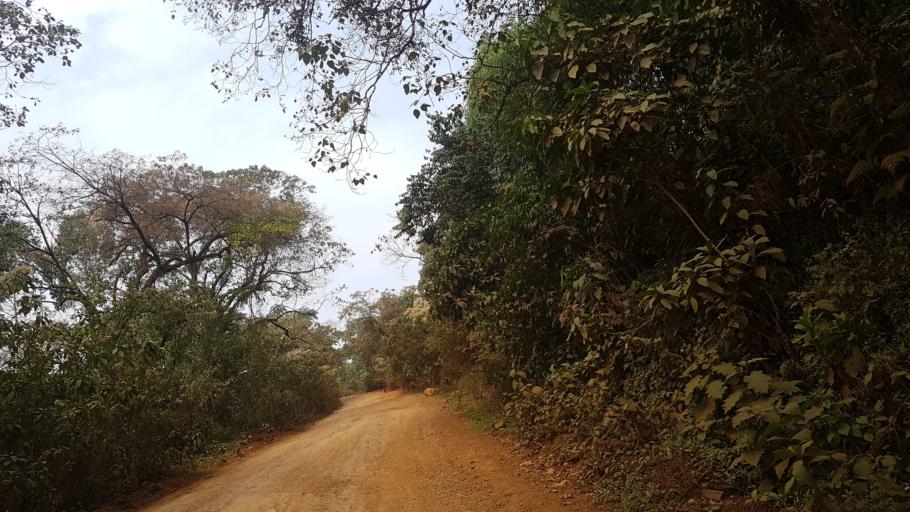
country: ET
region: Oromiya
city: Gore
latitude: 7.8234
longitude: 35.4610
